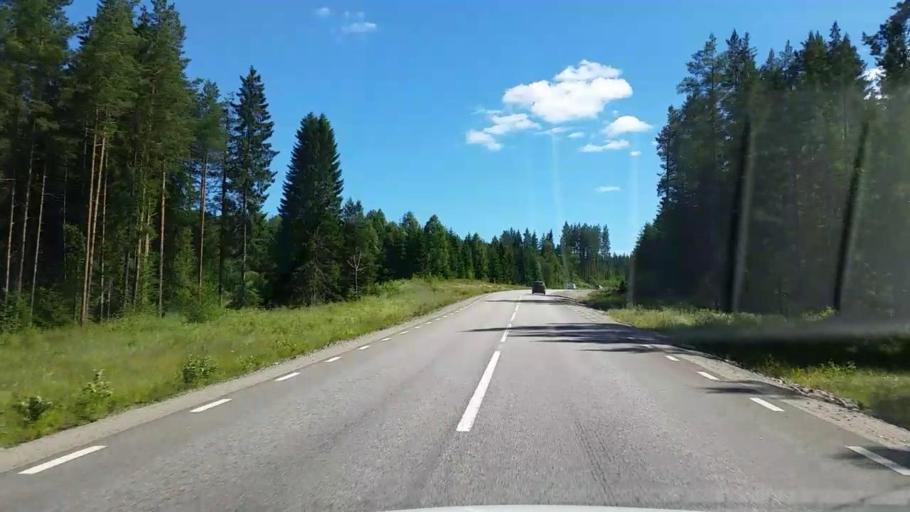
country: SE
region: Gaevleborg
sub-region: Ovanakers Kommun
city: Edsbyn
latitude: 61.1772
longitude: 15.8817
